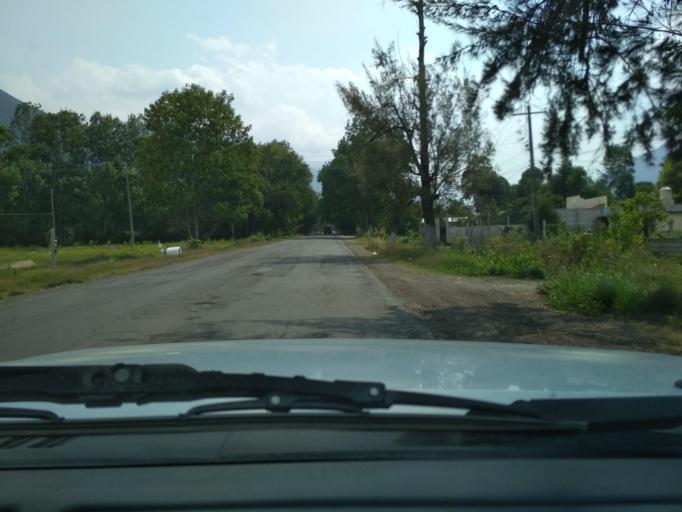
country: MX
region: Veracruz
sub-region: Acultzingo
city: Sierra de Agua
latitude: 18.7580
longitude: -97.2311
